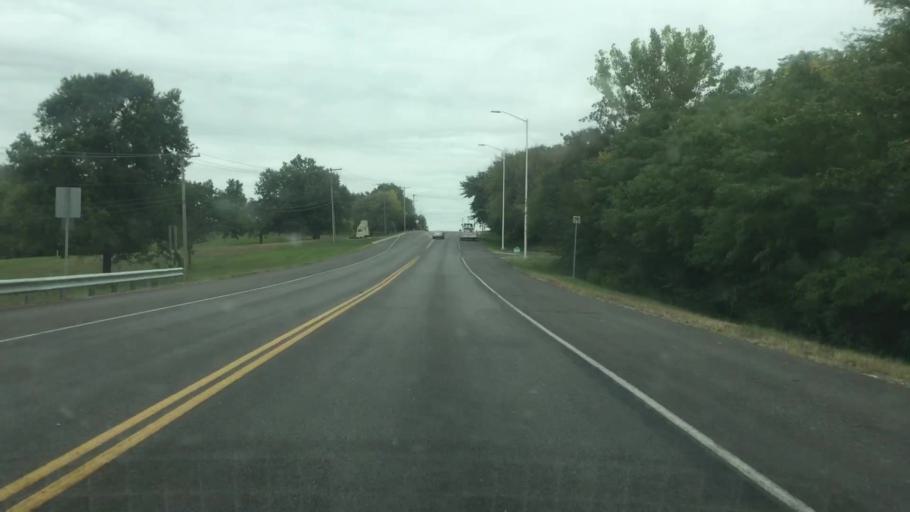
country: US
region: Kansas
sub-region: Johnson County
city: Lenexa
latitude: 38.9824
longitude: -94.7795
